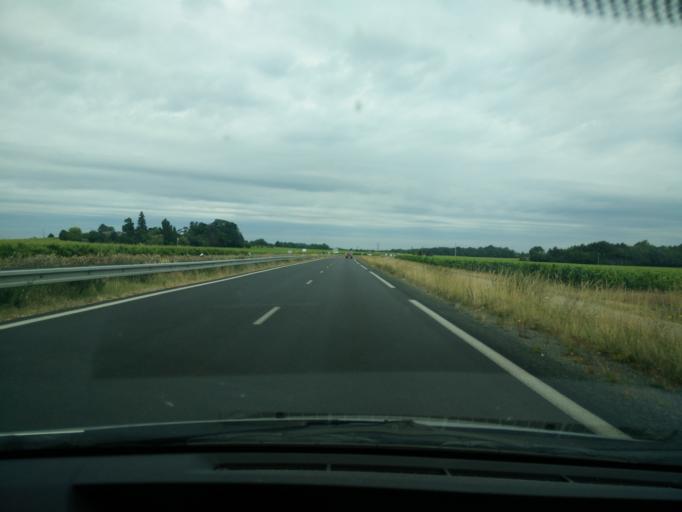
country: FR
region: Pays de la Loire
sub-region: Departement de Maine-et-Loire
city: Brissac-Quince
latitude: 47.3757
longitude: -0.4698
